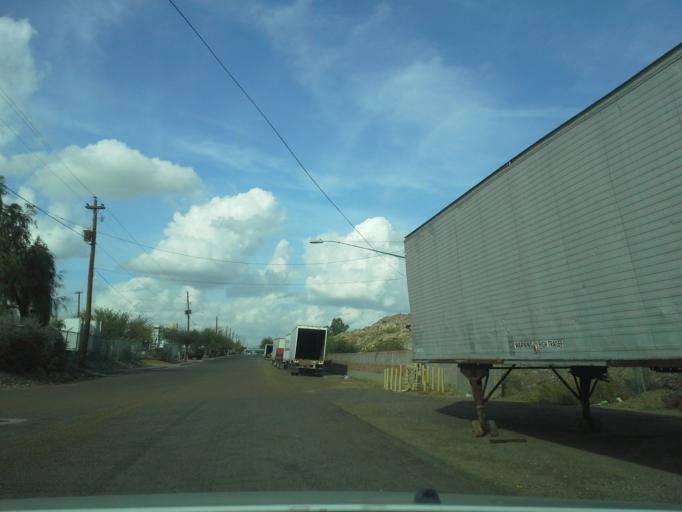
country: US
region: Arizona
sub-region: Maricopa County
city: Phoenix
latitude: 33.4220
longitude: -112.0911
